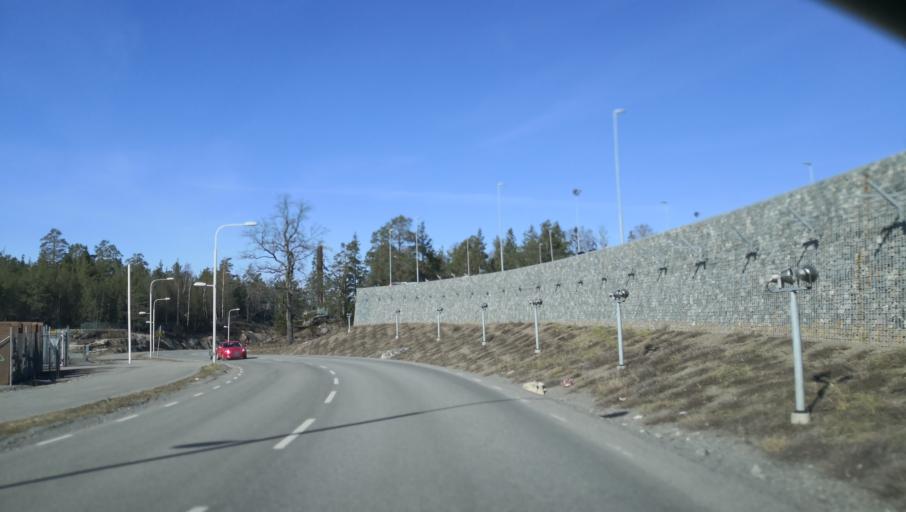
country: SE
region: Stockholm
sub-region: Varmdo Kommun
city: Gustavsberg
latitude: 59.3099
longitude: 18.3803
